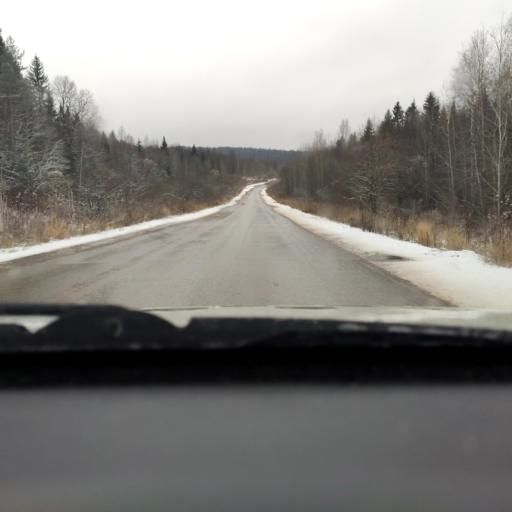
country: RU
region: Perm
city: Ferma
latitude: 57.9804
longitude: 56.3587
